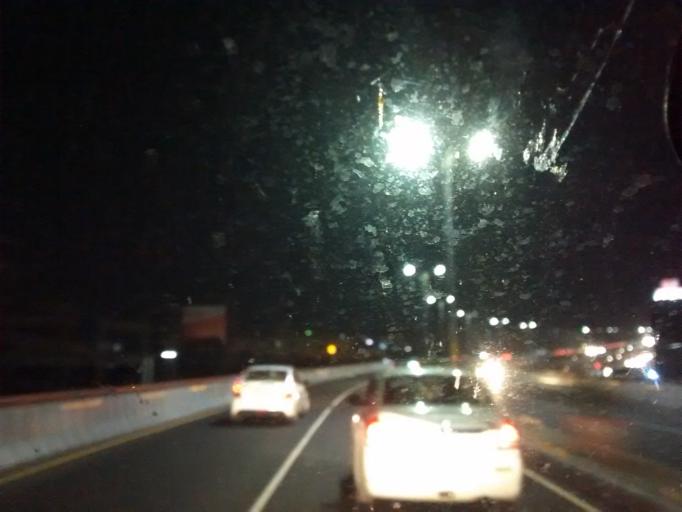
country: IN
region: Telangana
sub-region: Hyderabad
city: Hyderabad
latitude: 17.3511
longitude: 78.4175
